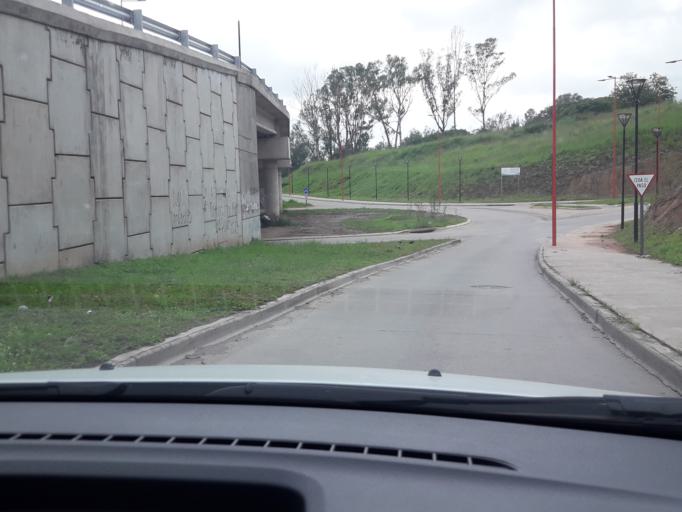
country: AR
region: Jujuy
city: San Salvador de Jujuy
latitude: -24.1793
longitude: -65.3272
